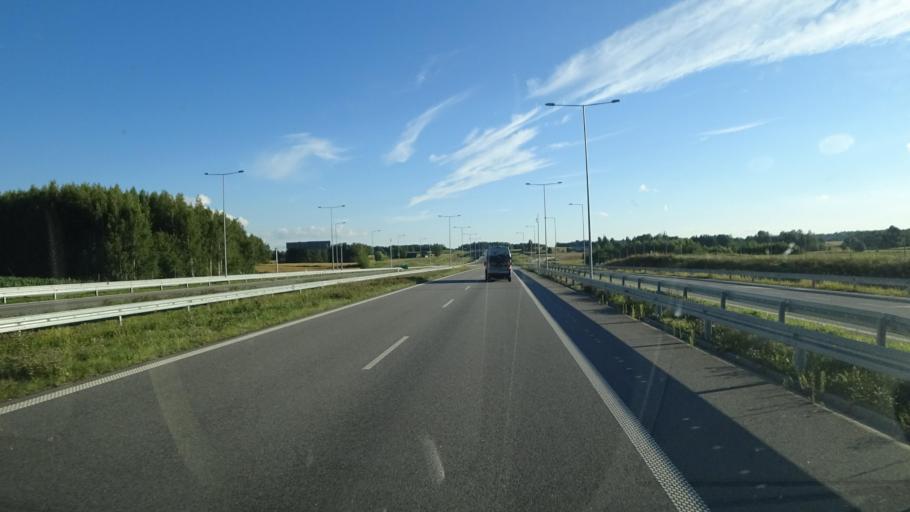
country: PL
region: Podlasie
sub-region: Powiat suwalski
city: Raczki
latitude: 53.9691
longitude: 22.7831
